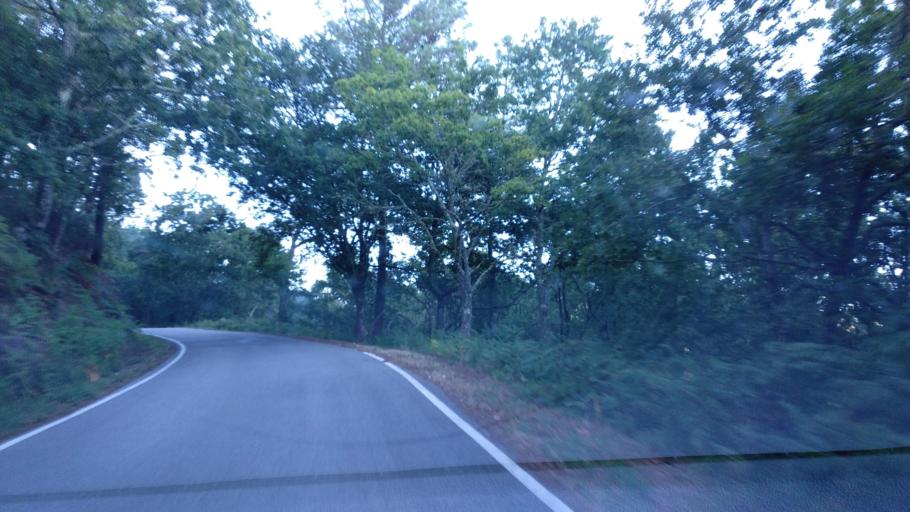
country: ES
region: Galicia
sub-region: Provincia de Pontevedra
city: Fornelos de Montes
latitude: 42.3511
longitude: -8.4899
